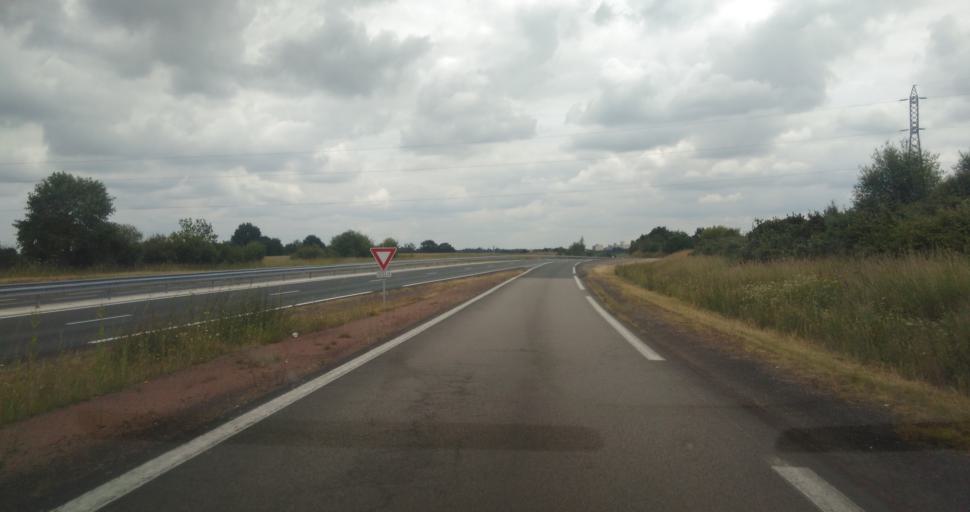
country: FR
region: Pays de la Loire
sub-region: Departement de la Vendee
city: La Chaize-le-Vicomte
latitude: 46.6628
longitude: -1.2651
